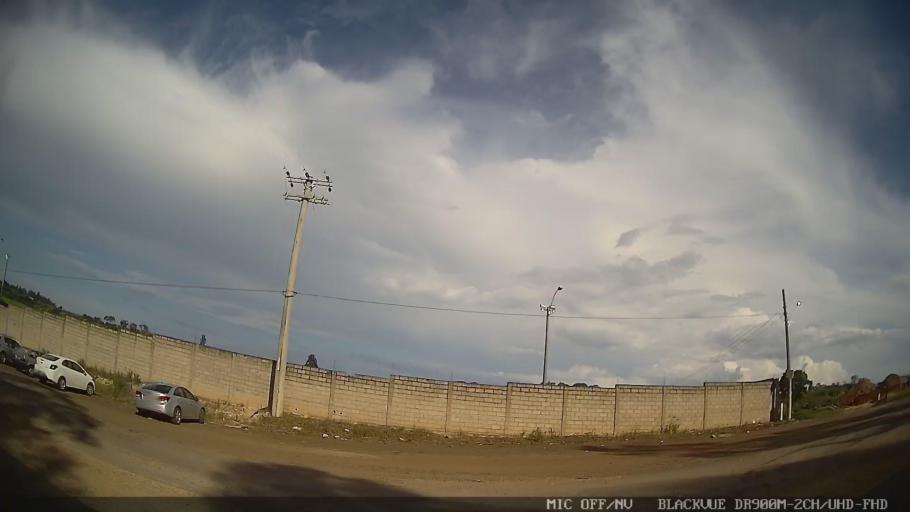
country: BR
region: Sao Paulo
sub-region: Tiete
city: Tiete
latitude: -23.1147
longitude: -47.6981
